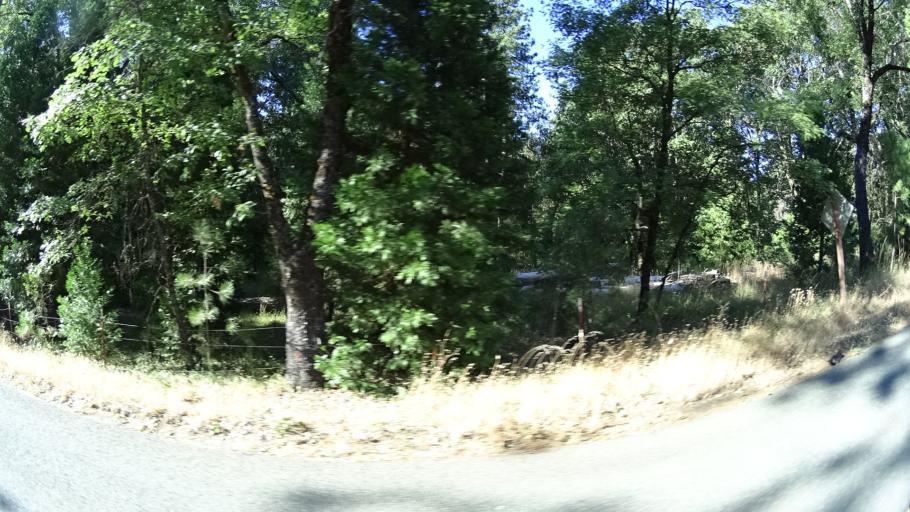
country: US
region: California
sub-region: Amador County
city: Pioneer
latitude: 38.3883
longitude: -120.5408
